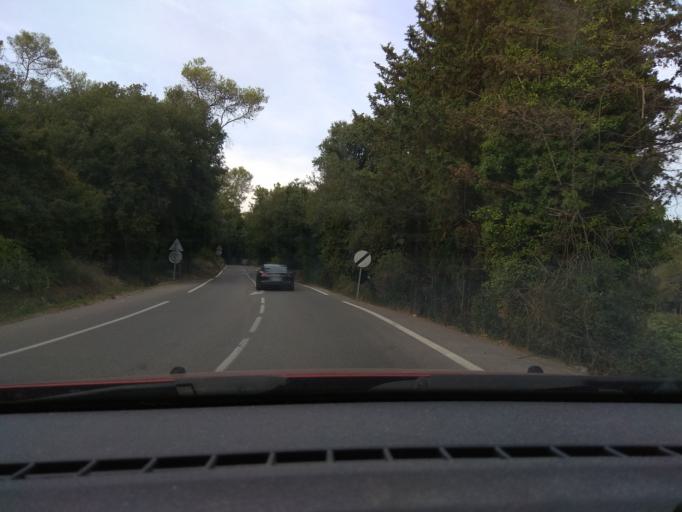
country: FR
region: Provence-Alpes-Cote d'Azur
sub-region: Departement des Alpes-Maritimes
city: Le Rouret
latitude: 43.6557
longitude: 7.0261
